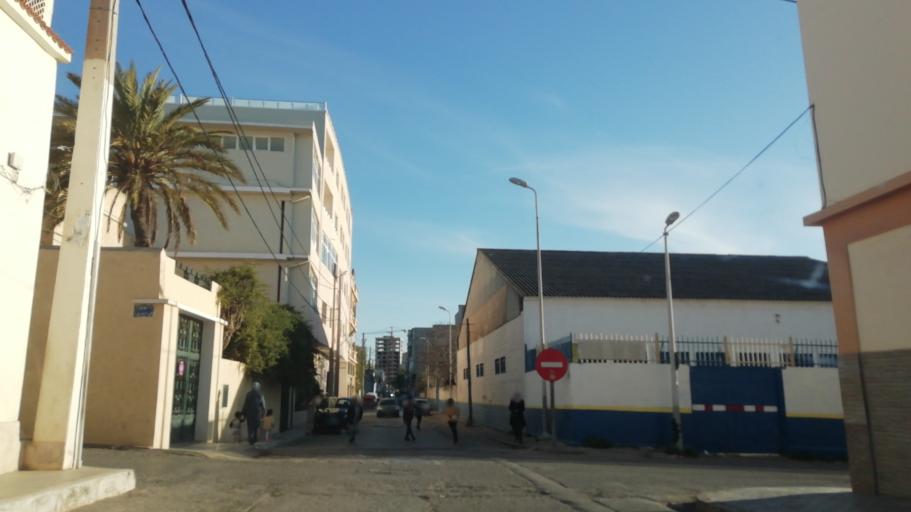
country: DZ
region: Oran
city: Oran
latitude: 35.7097
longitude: -0.6086
